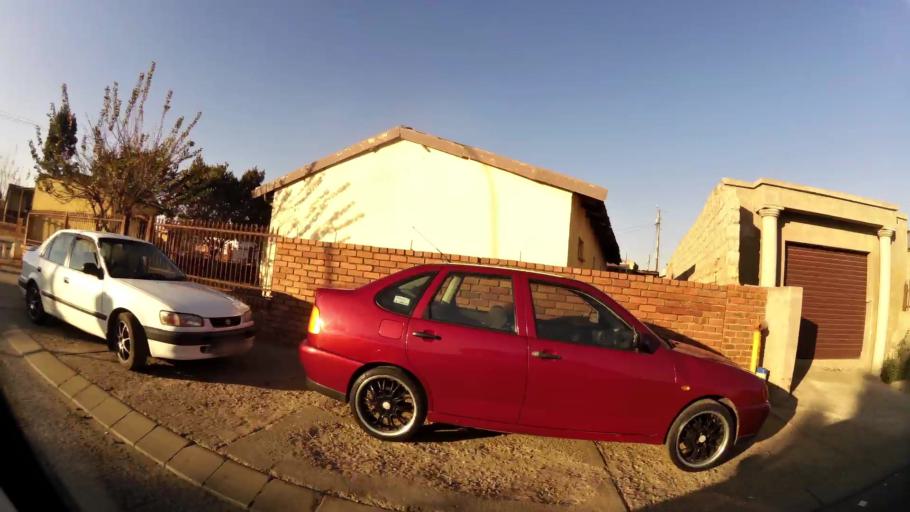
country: ZA
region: Gauteng
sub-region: City of Tshwane Metropolitan Municipality
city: Cullinan
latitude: -25.7237
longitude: 28.3801
